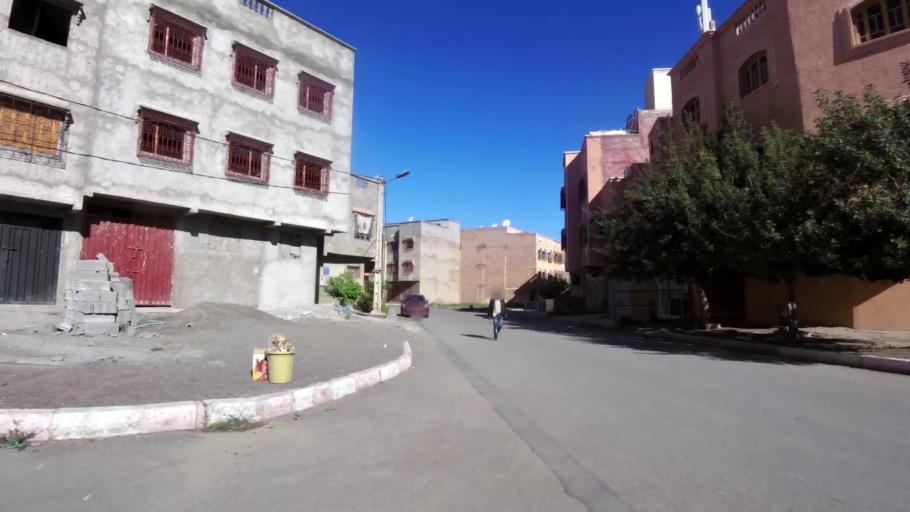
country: MA
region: Marrakech-Tensift-Al Haouz
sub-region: Marrakech
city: Marrakesh
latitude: 31.6007
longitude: -8.0359
